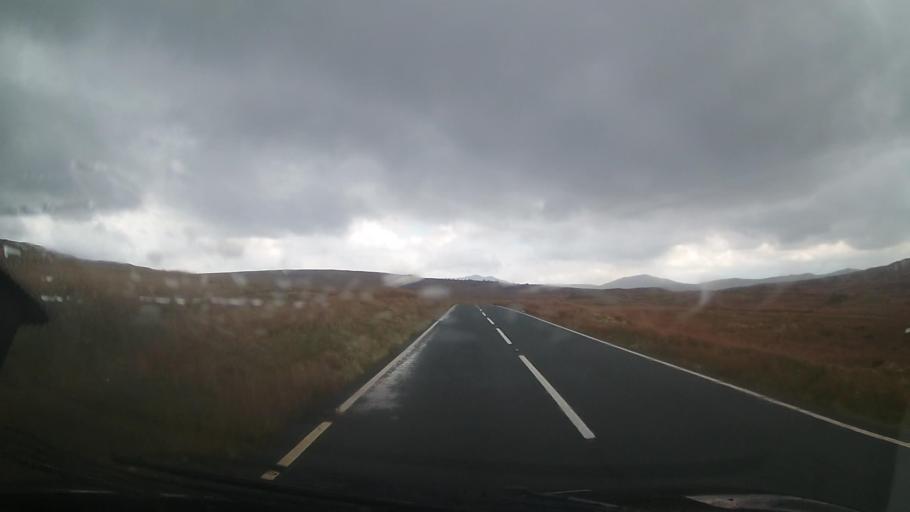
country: GB
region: Wales
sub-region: Gwynedd
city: Ffestiniog
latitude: 52.9542
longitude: -3.8529
